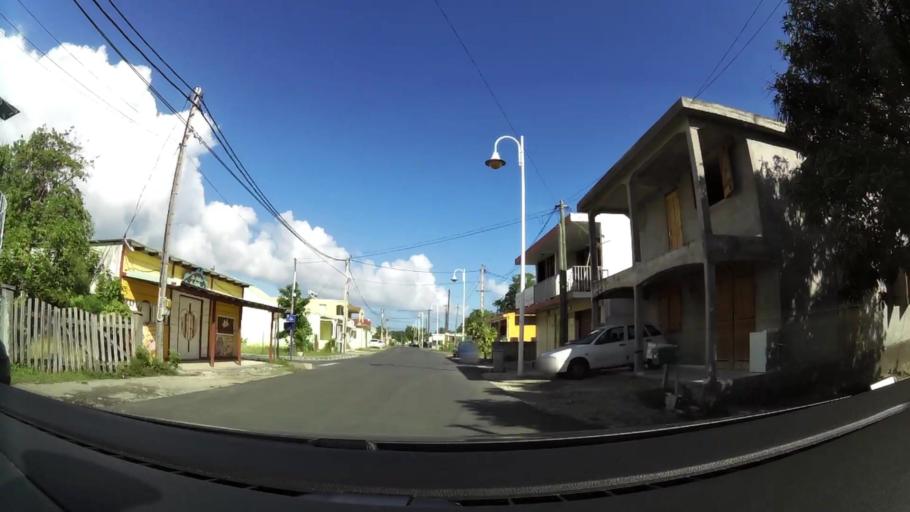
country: GP
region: Guadeloupe
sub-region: Guadeloupe
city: Sainte-Anne
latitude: 16.2252
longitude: -61.3803
